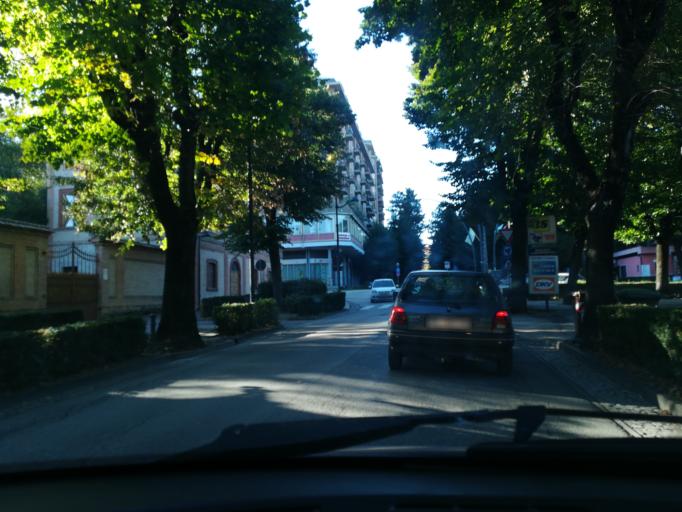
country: IT
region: The Marches
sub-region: Provincia di Macerata
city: Tolentino
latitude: 43.2108
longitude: 13.2870
